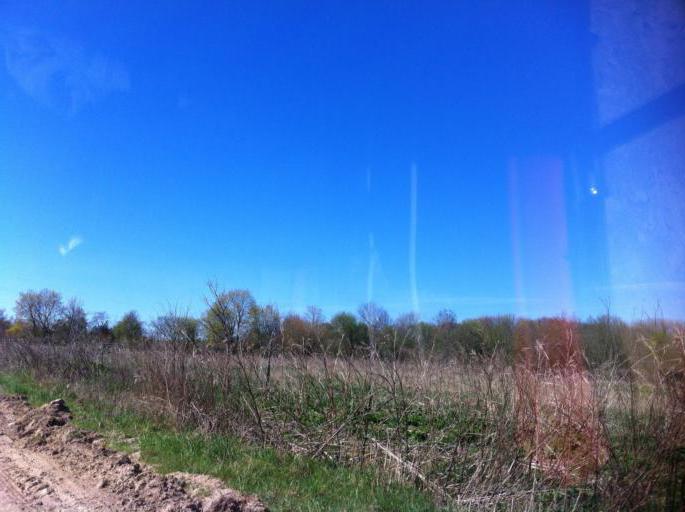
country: RU
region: Pskov
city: Izborsk
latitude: 57.8086
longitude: 27.9787
